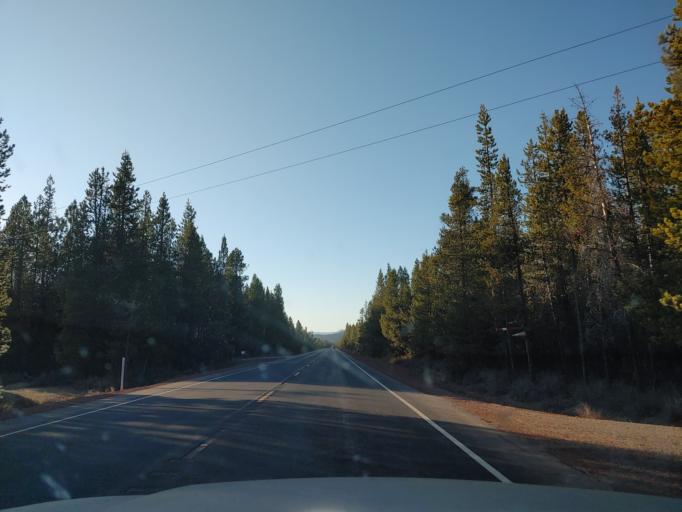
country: US
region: Oregon
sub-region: Deschutes County
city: La Pine
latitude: 43.3961
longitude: -121.8167
